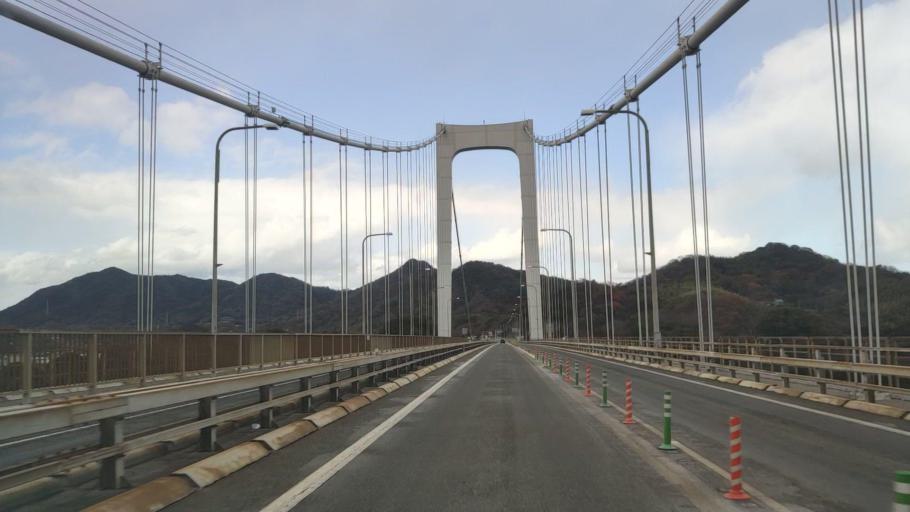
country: JP
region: Hiroshima
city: Innoshima
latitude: 34.1928
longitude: 133.0730
